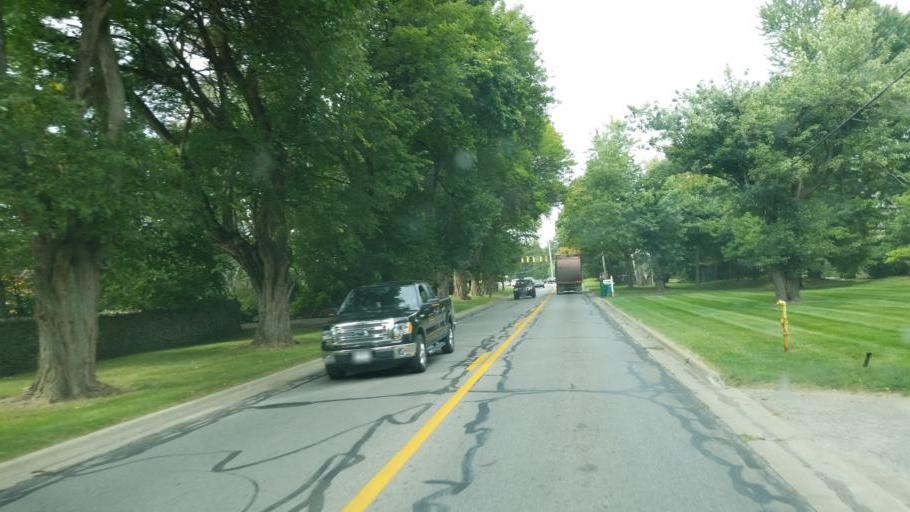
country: US
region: Ohio
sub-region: Franklin County
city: New Albany
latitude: 40.0423
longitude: -82.8095
